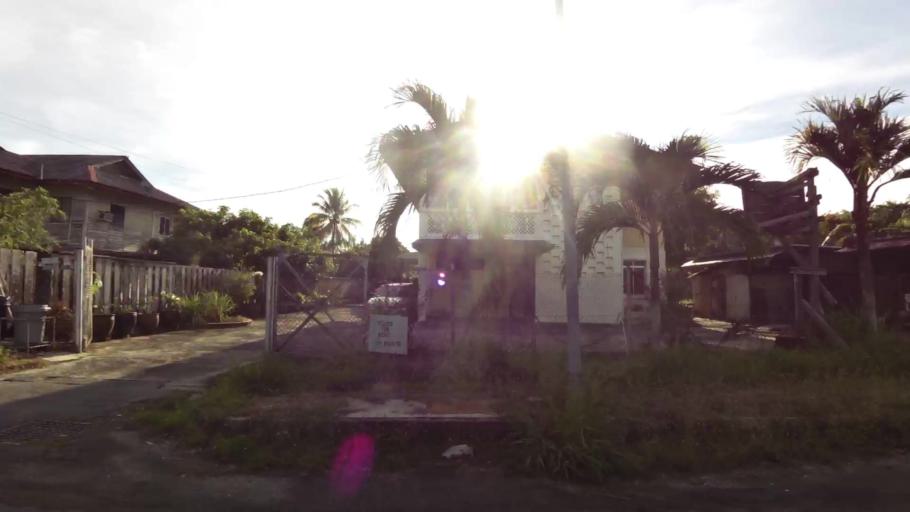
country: BN
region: Belait
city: Kuala Belait
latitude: 4.5857
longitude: 114.1961
